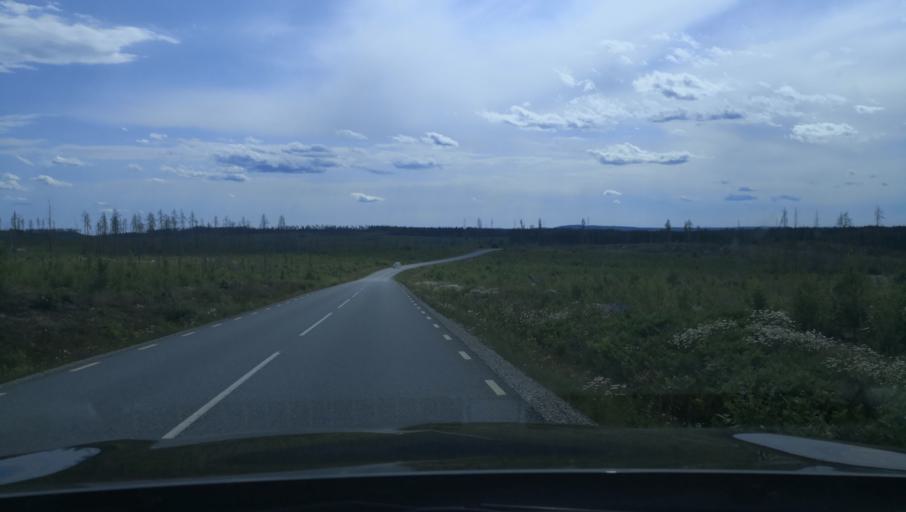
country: SE
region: Vaestmanland
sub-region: Norbergs Kommun
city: Norberg
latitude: 59.9802
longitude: 16.0448
